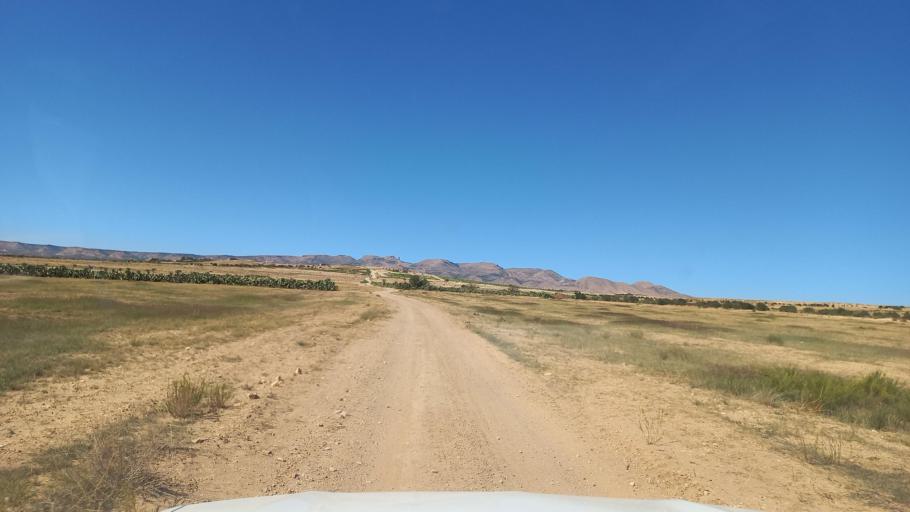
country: TN
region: Al Qasrayn
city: Sbiba
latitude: 35.3704
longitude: 9.0841
